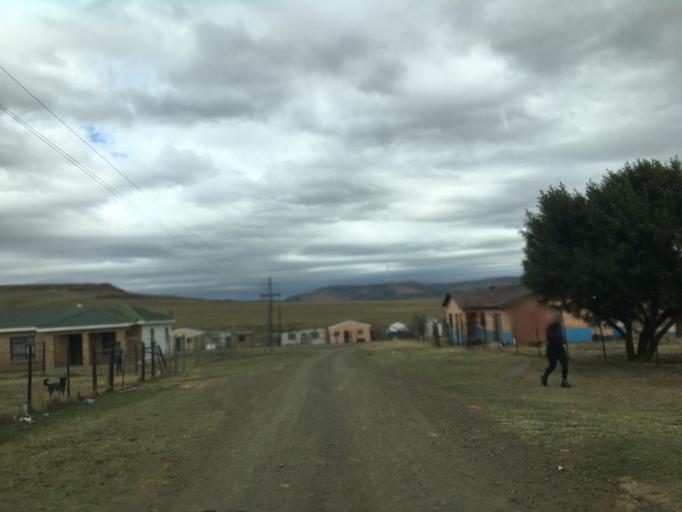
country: ZA
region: Eastern Cape
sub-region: Chris Hani District Municipality
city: Cala
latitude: -31.5407
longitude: 27.6975
